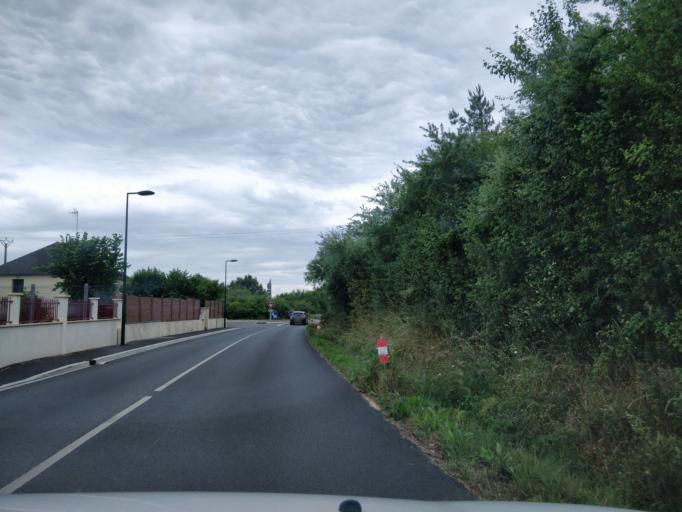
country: FR
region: Pays de la Loire
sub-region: Departement de Maine-et-Loire
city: Feneu
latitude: 47.5667
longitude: -0.5873
